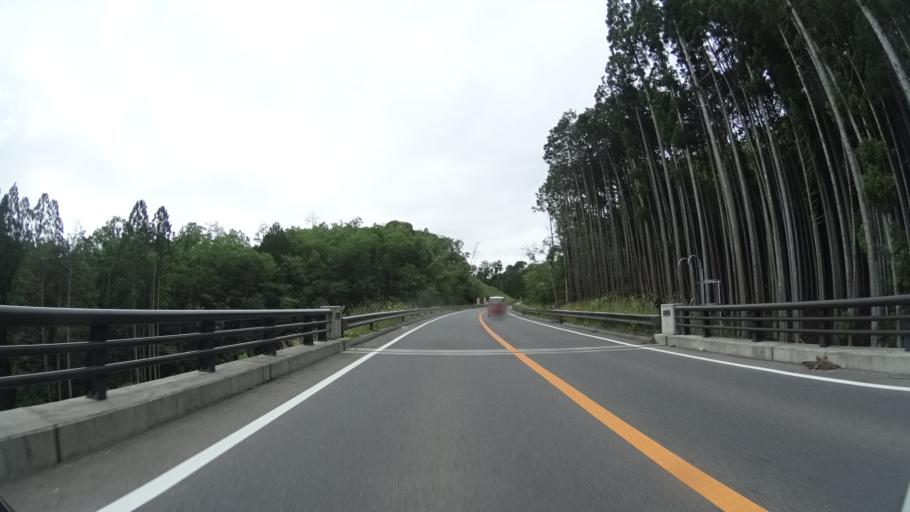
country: JP
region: Mie
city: Ueno-ebisumachi
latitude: 34.7740
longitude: 136.0003
